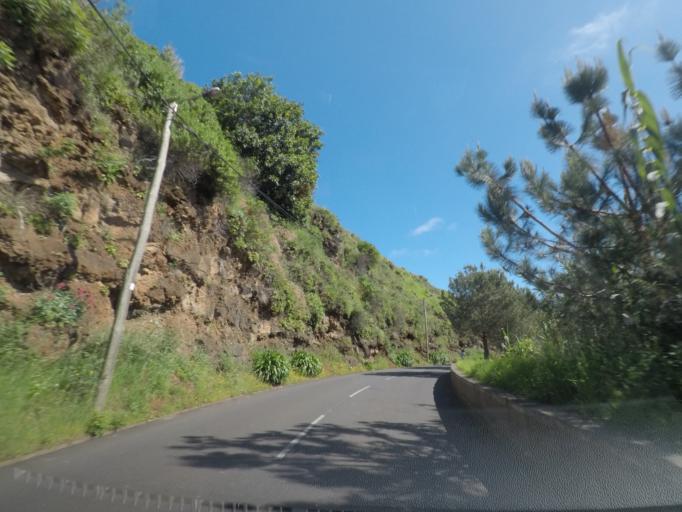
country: PT
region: Madeira
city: Ponta do Sol
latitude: 32.7008
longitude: -17.1068
